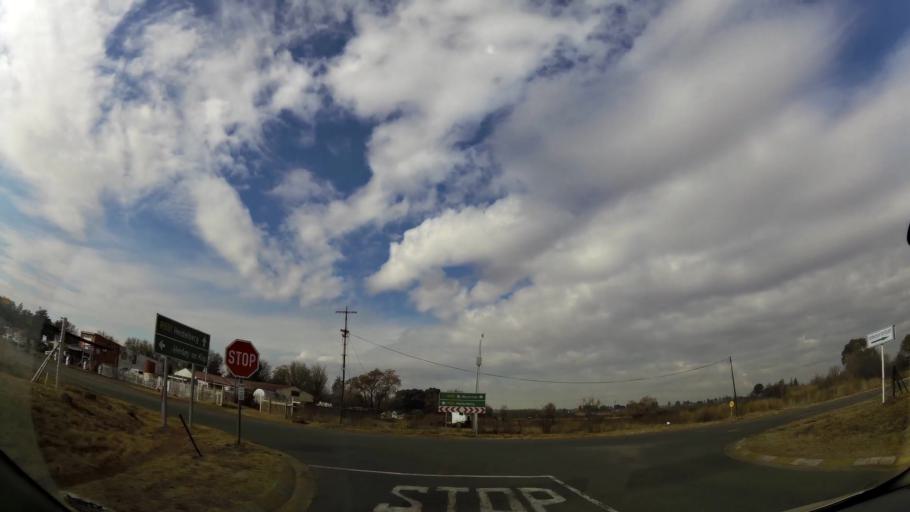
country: ZA
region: Gauteng
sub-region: Sedibeng District Municipality
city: Meyerton
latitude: -26.5574
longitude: 28.0616
